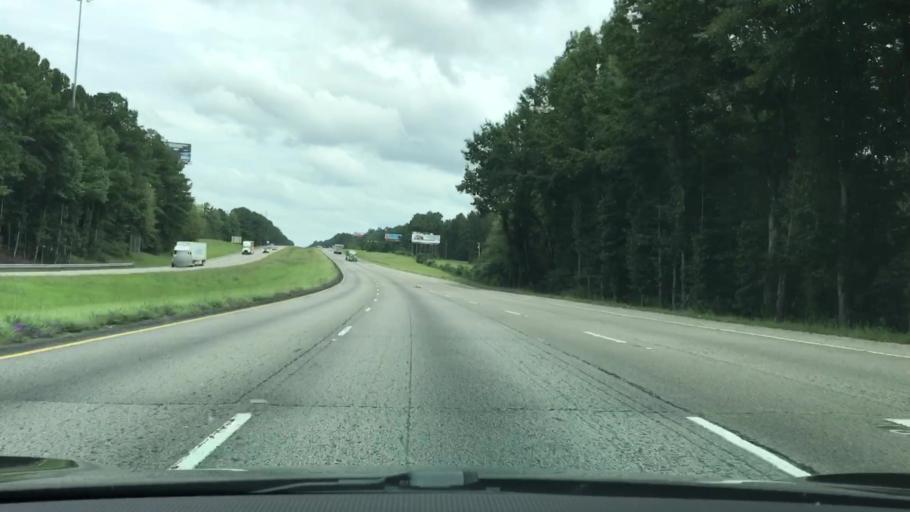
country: US
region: Georgia
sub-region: Troup County
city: West Point
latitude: 32.8808
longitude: -85.1473
